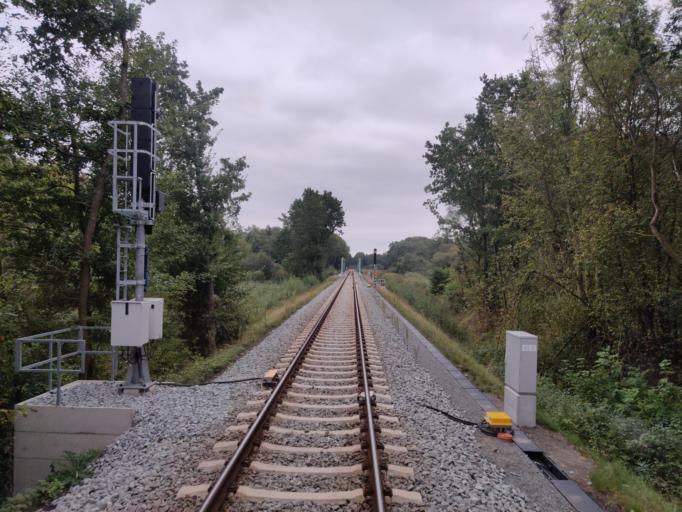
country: DE
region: Lower Saxony
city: Bremervorde
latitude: 53.4803
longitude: 9.1488
